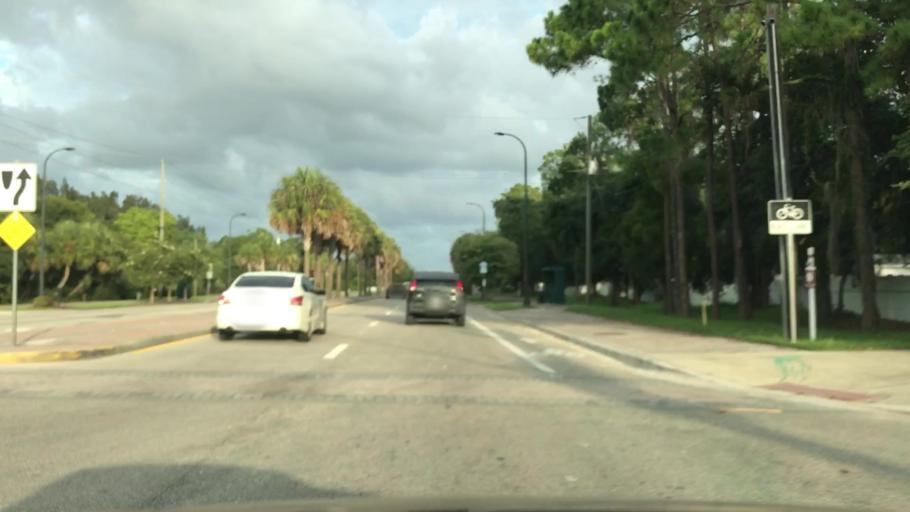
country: US
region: Florida
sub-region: Sarasota County
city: Fruitville
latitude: 27.3383
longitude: -82.4167
